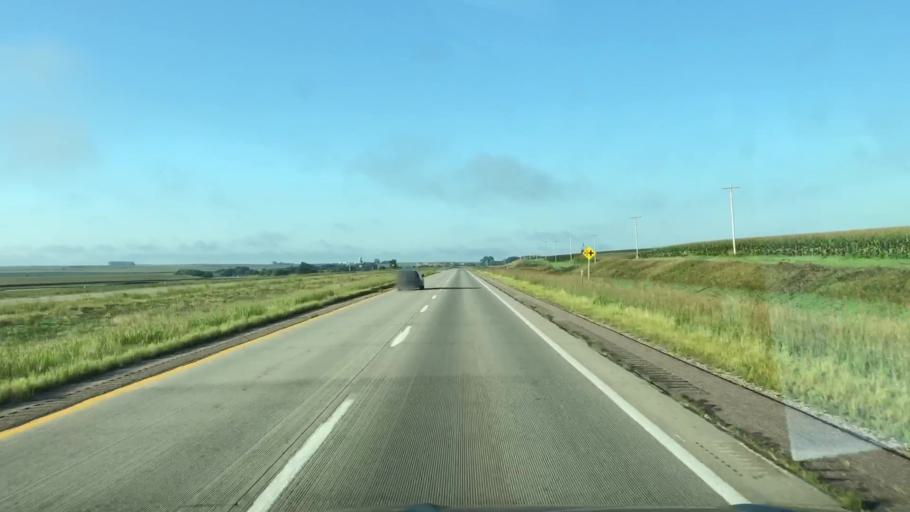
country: US
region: Iowa
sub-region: Sioux County
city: Alton
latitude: 42.9416
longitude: -96.0426
